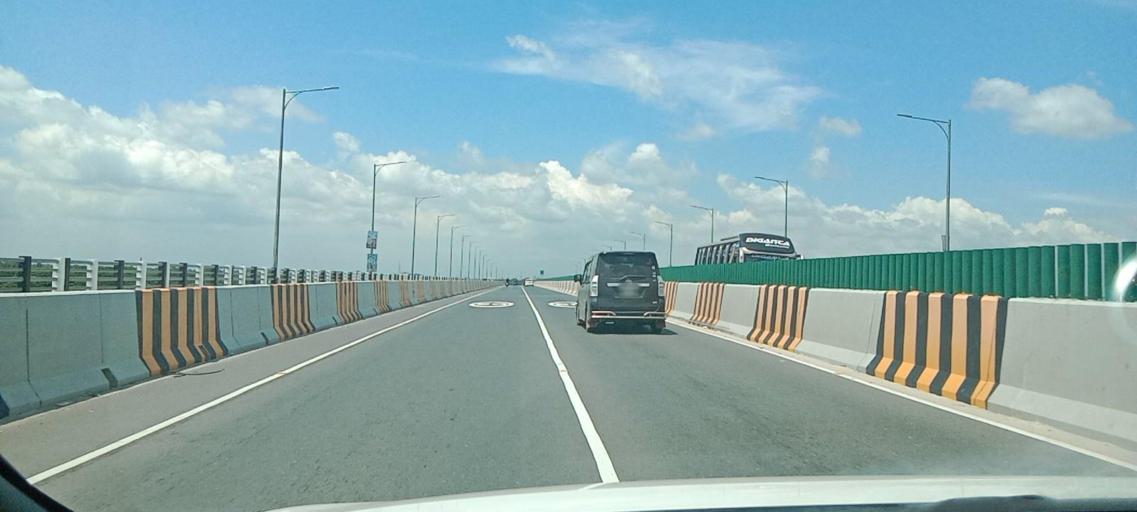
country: BD
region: Dhaka
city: Dohar
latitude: 23.5140
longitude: 90.2778
